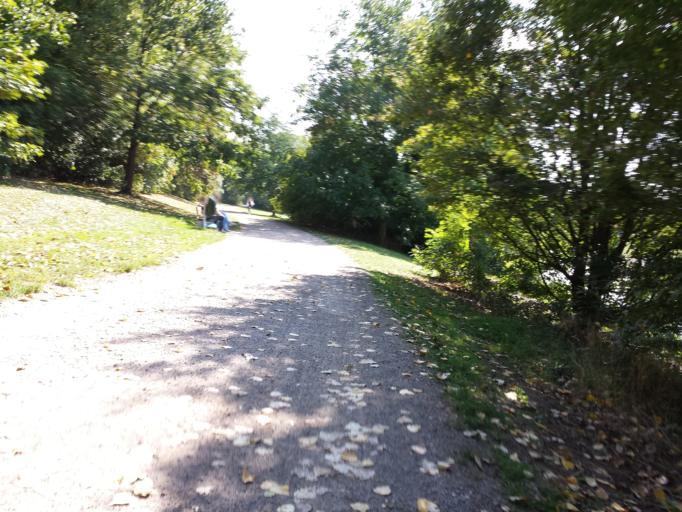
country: DE
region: Bremen
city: Bremen
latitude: 53.0653
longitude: 8.8100
